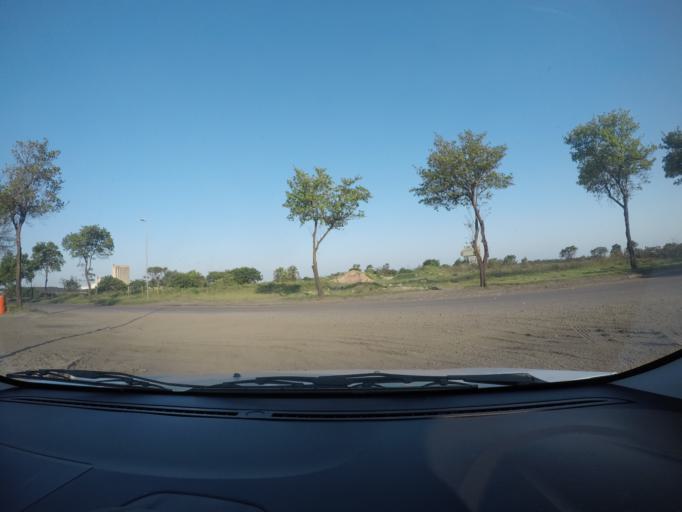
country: ZA
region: KwaZulu-Natal
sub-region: uThungulu District Municipality
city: Richards Bay
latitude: -28.7613
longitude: 32.0075
